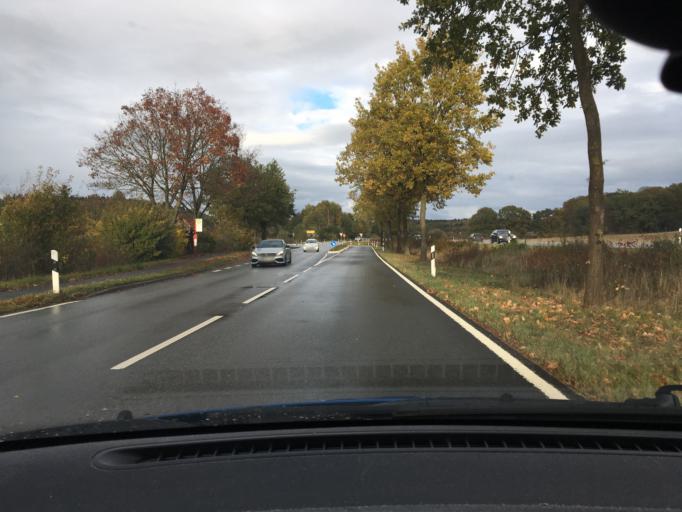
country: DE
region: Schleswig-Holstein
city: Fredeburg
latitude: 53.6442
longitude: 10.7002
